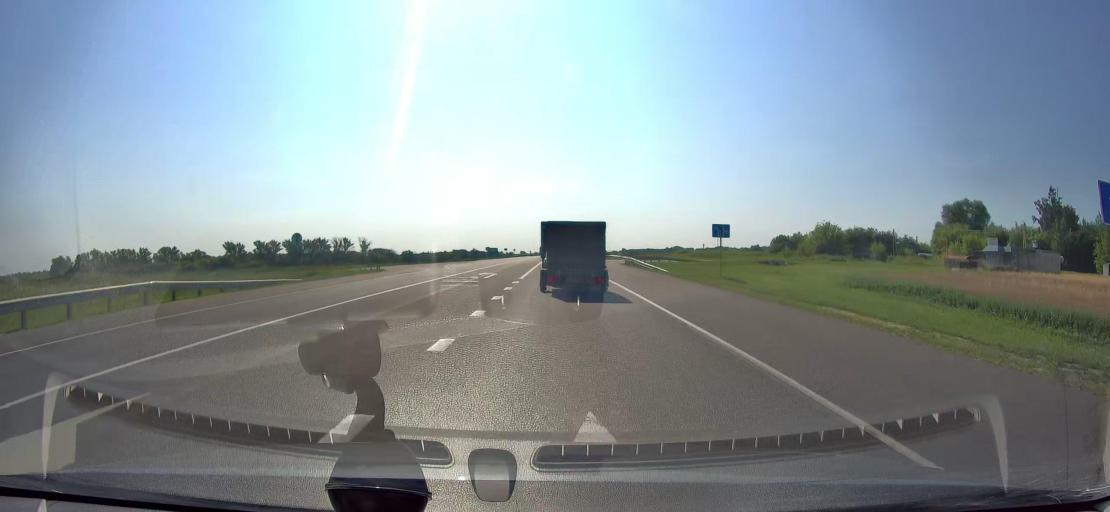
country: RU
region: Orjol
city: Kromy
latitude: 52.6504
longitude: 35.7347
